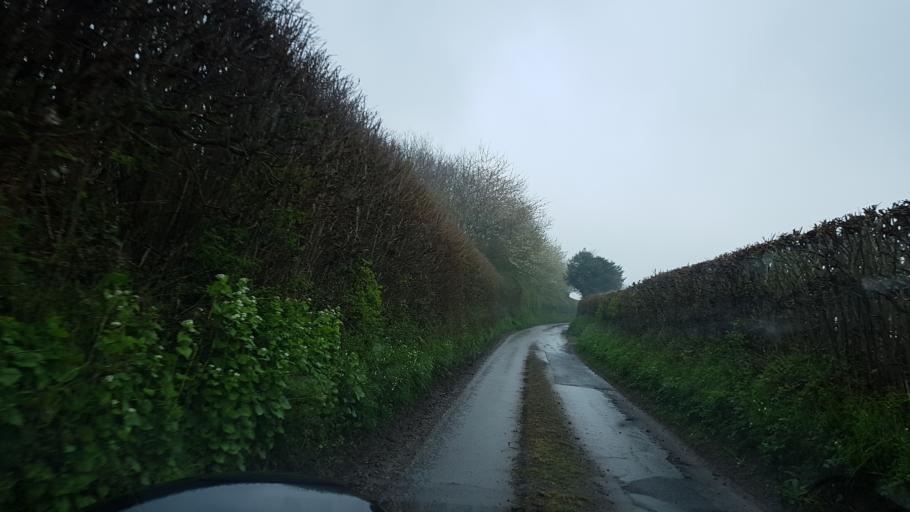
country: GB
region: England
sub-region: Herefordshire
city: Sellack
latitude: 51.9651
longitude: -2.6395
